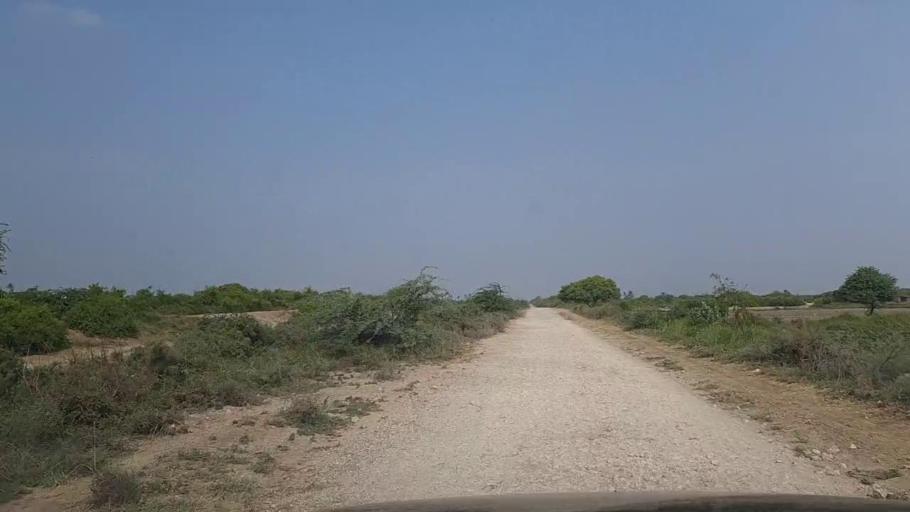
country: PK
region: Sindh
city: Thatta
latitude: 24.7492
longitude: 67.8079
